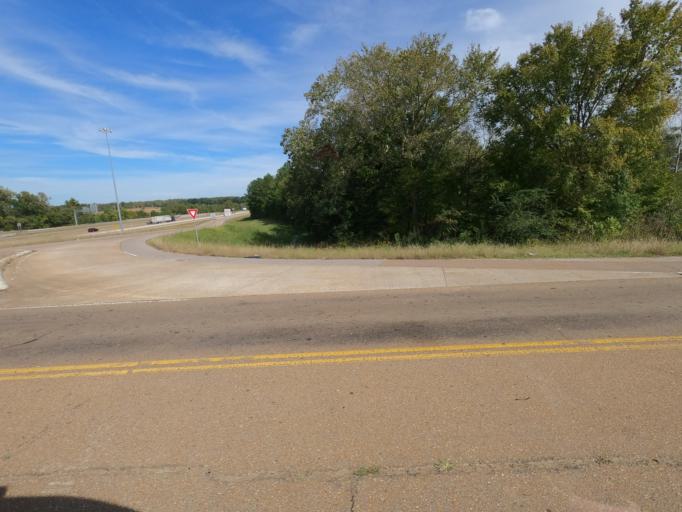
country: US
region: Tennessee
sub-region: Shelby County
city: Arlington
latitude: 35.2614
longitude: -89.6644
